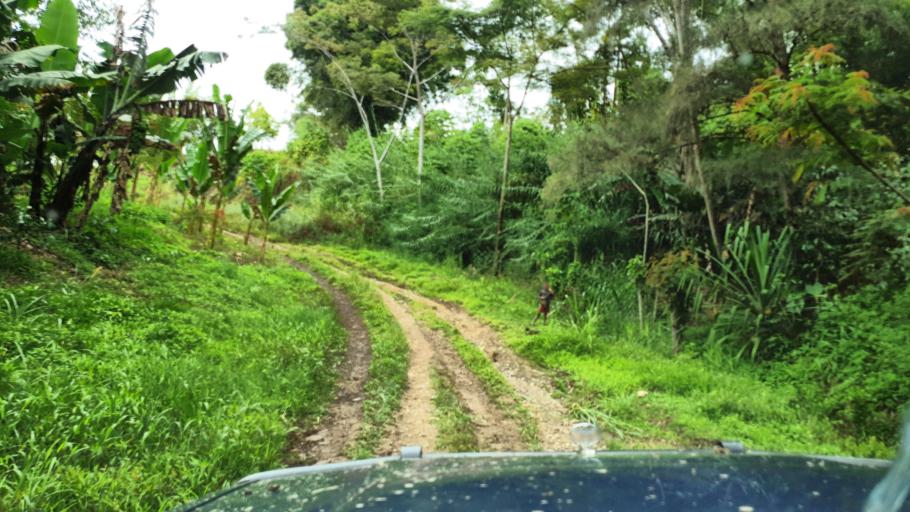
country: PG
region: Jiwaka
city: Minj
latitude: -5.9318
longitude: 144.7521
